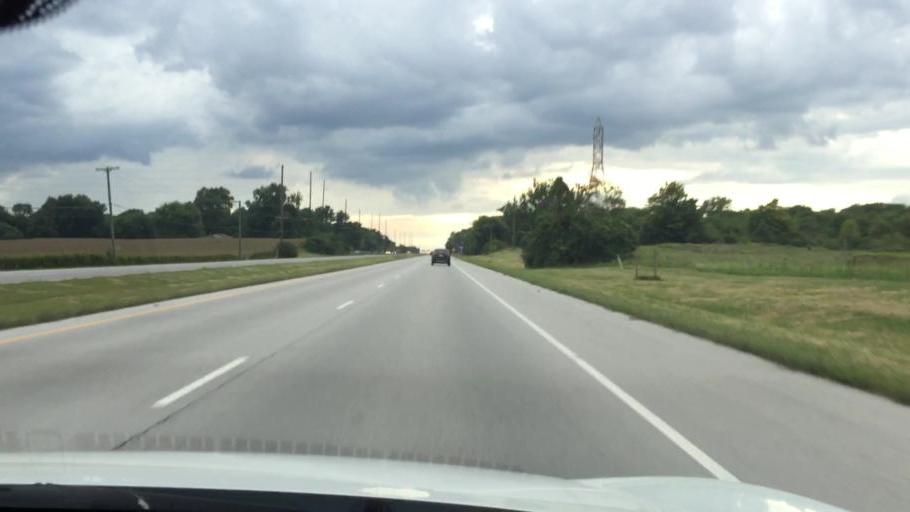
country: US
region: Ohio
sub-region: Clark County
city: Springfield
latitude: 39.9233
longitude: -83.7304
